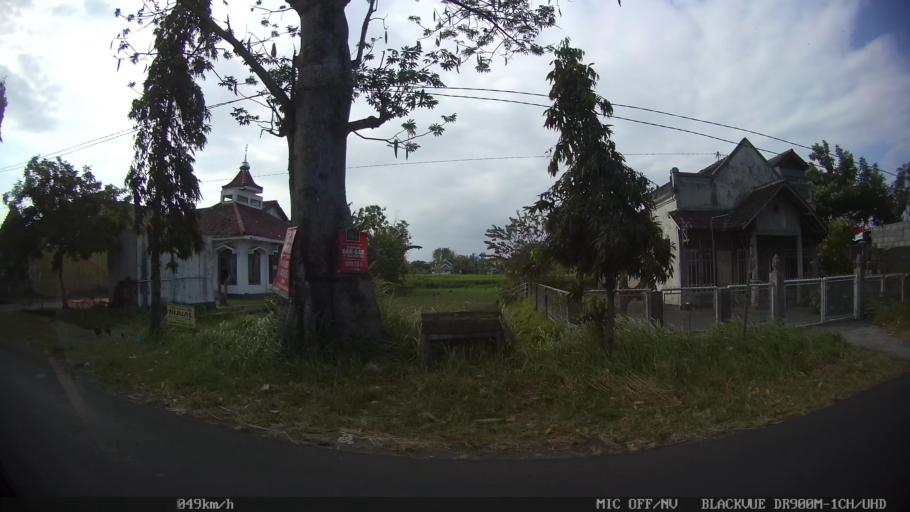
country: ID
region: Daerah Istimewa Yogyakarta
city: Sewon
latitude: -7.8671
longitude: 110.3423
